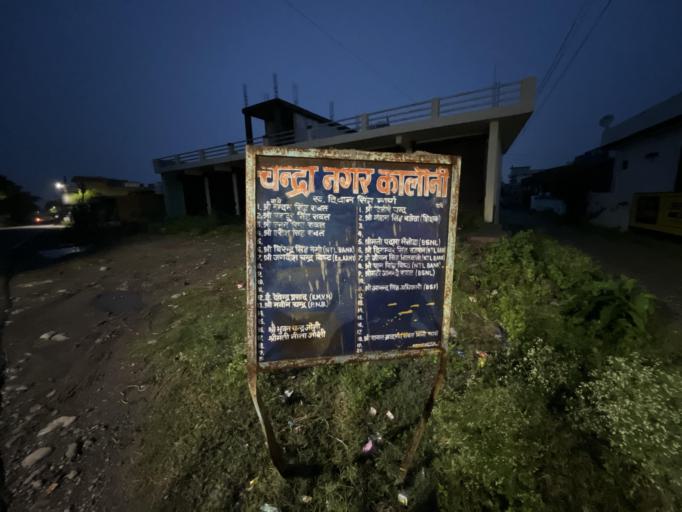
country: IN
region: Uttarakhand
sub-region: Naini Tal
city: Haldwani
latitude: 29.2044
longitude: 79.4913
